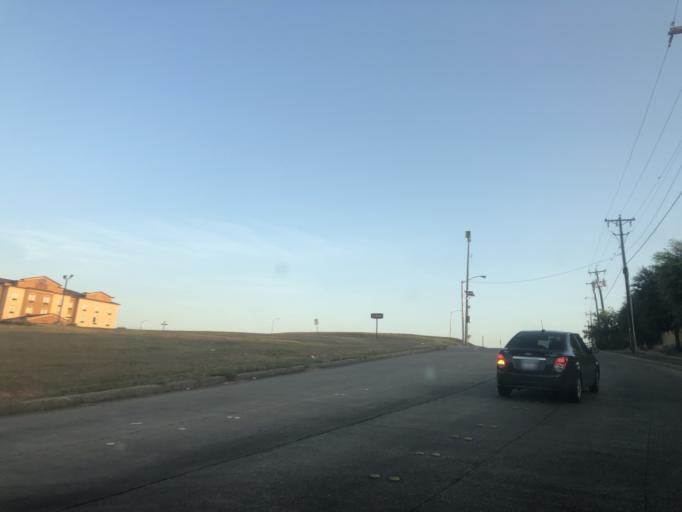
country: US
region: Texas
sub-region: Tarrant County
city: Lake Worth
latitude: 32.8020
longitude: -97.4248
